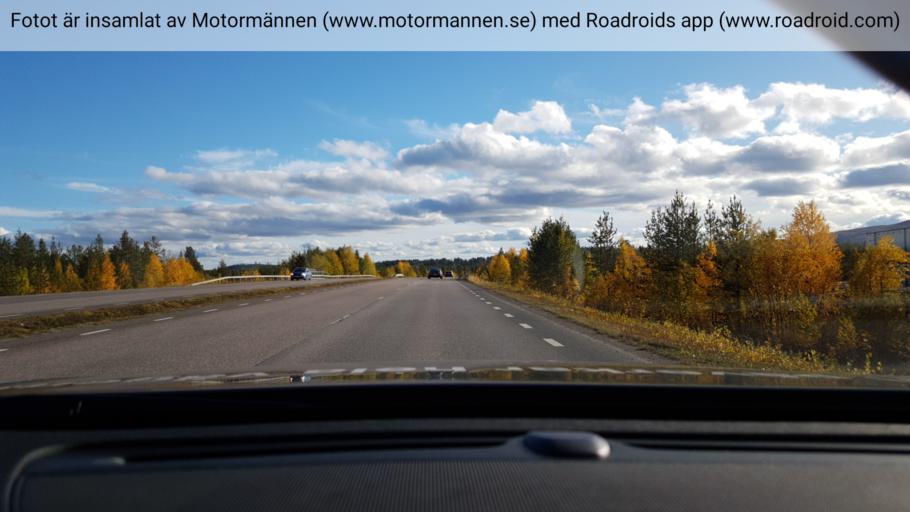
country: SE
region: Norrbotten
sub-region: Gallivare Kommun
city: Malmberget
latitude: 67.1576
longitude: 20.6600
